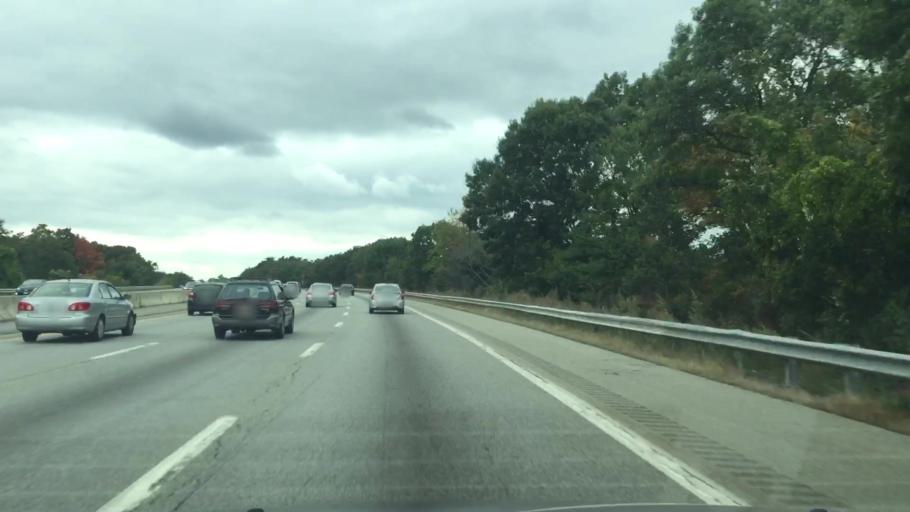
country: US
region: Massachusetts
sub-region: Middlesex County
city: Cochituate
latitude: 42.3163
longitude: -71.3571
